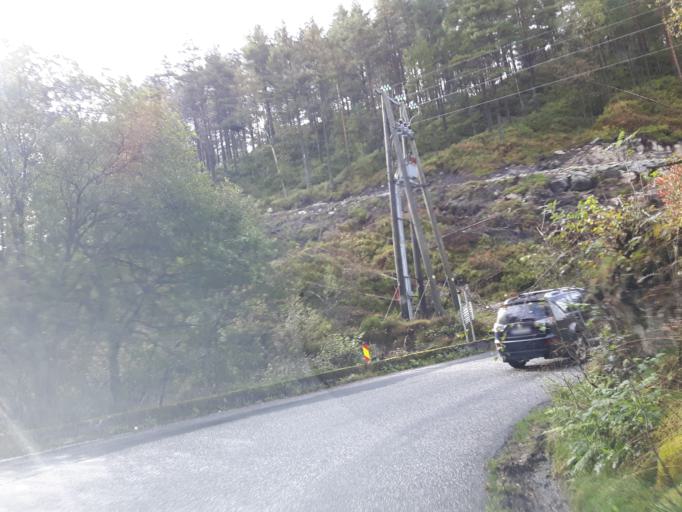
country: NO
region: Rogaland
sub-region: Lund
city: Moi
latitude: 58.3959
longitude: 6.6298
